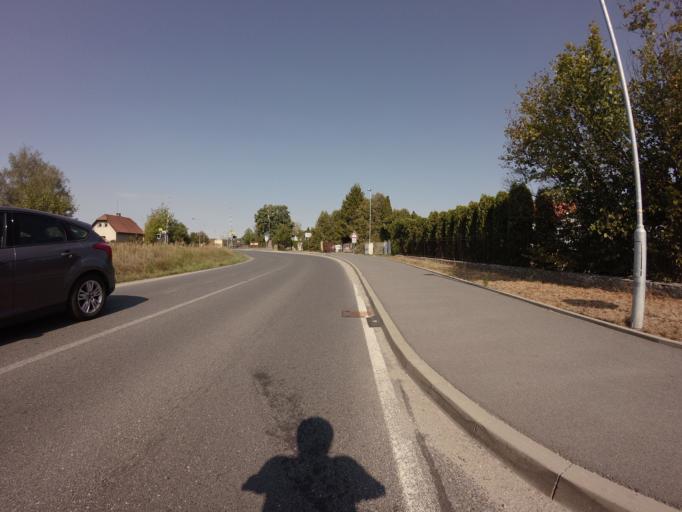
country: CZ
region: Central Bohemia
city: Tynec nad Sazavou
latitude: 49.8391
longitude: 14.5785
